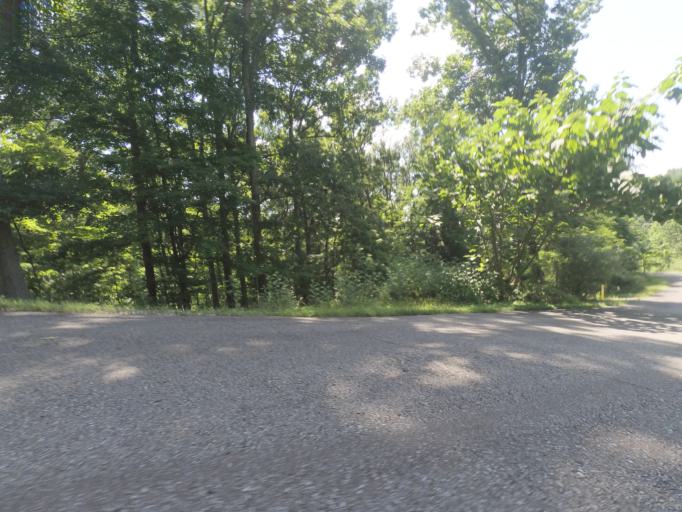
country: US
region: West Virginia
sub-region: Cabell County
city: Huntington
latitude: 38.3831
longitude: -82.4643
